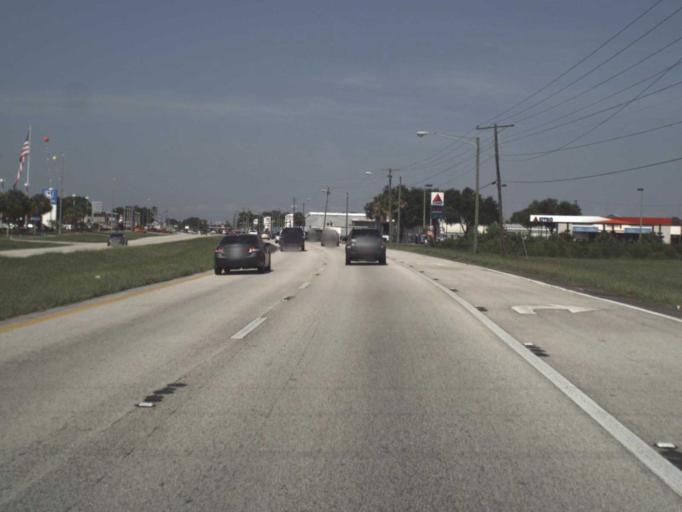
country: US
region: Florida
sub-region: Hillsborough County
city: Palm River-Clair Mel
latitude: 27.9499
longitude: -82.3479
